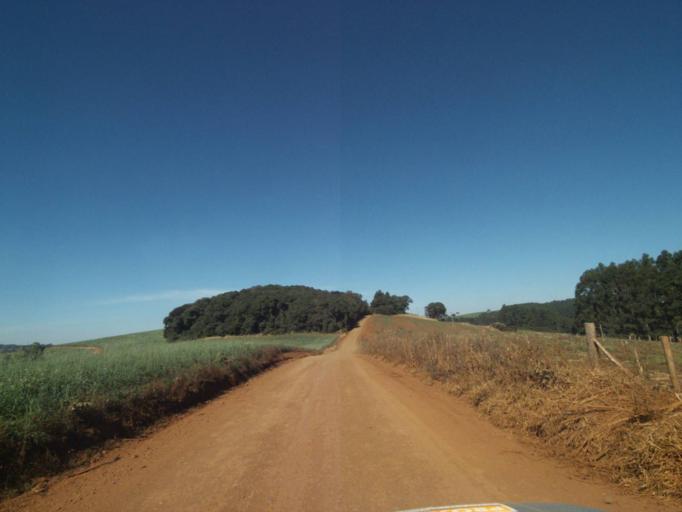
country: BR
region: Parana
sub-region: Tibagi
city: Tibagi
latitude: -24.5881
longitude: -50.6074
